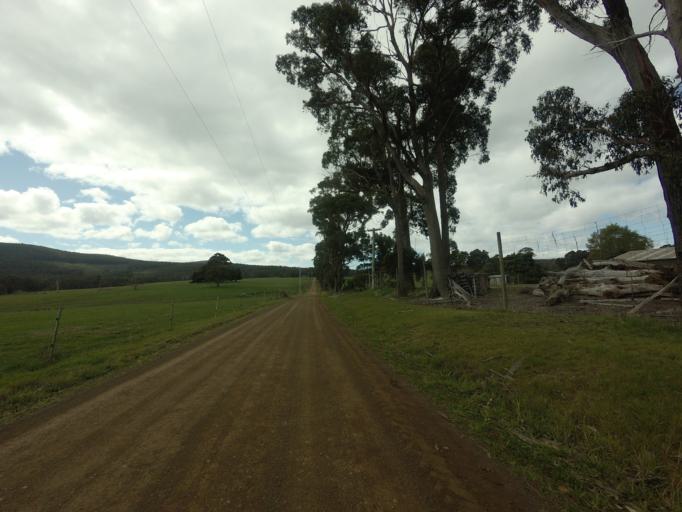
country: AU
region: Tasmania
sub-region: Huon Valley
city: Geeveston
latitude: -43.4340
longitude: 146.9873
